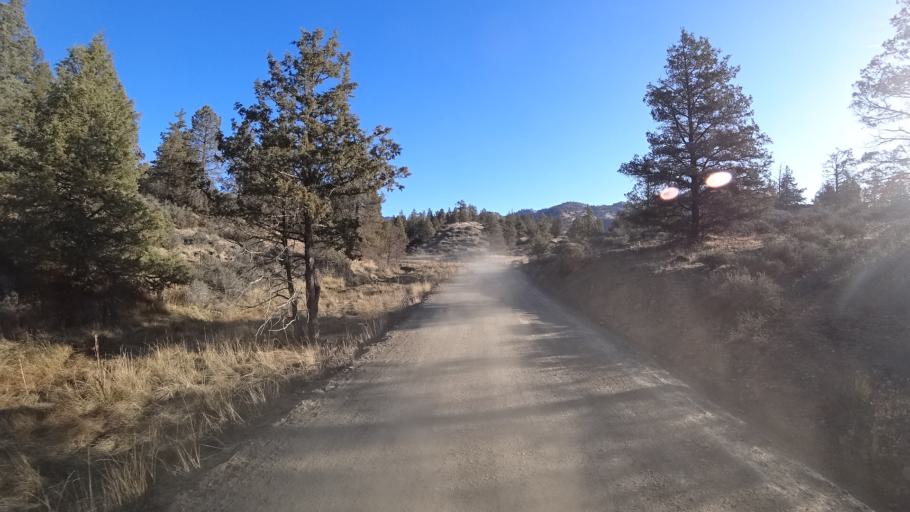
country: US
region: Oregon
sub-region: Jackson County
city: Ashland
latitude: 41.9865
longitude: -122.6226
